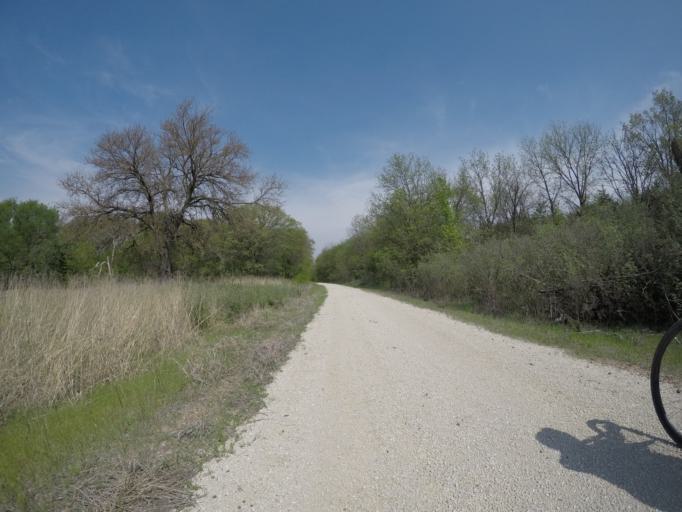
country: US
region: Nebraska
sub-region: Gage County
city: Wymore
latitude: 40.1210
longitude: -96.6368
